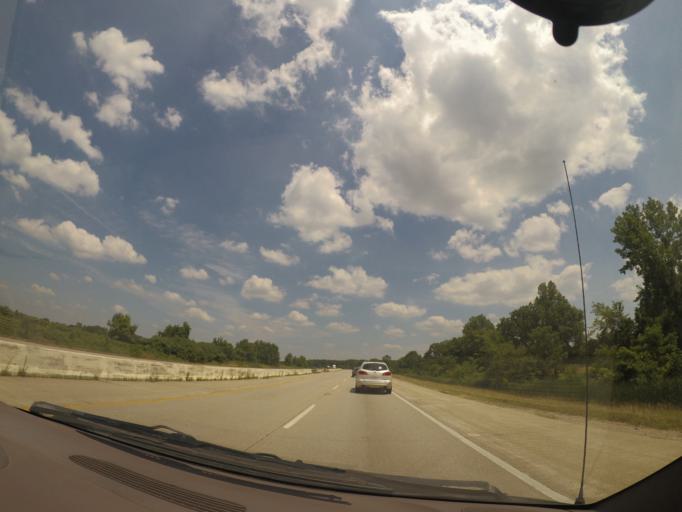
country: US
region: Indiana
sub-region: Saint Joseph County
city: Osceola
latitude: 41.6161
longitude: -86.0568
